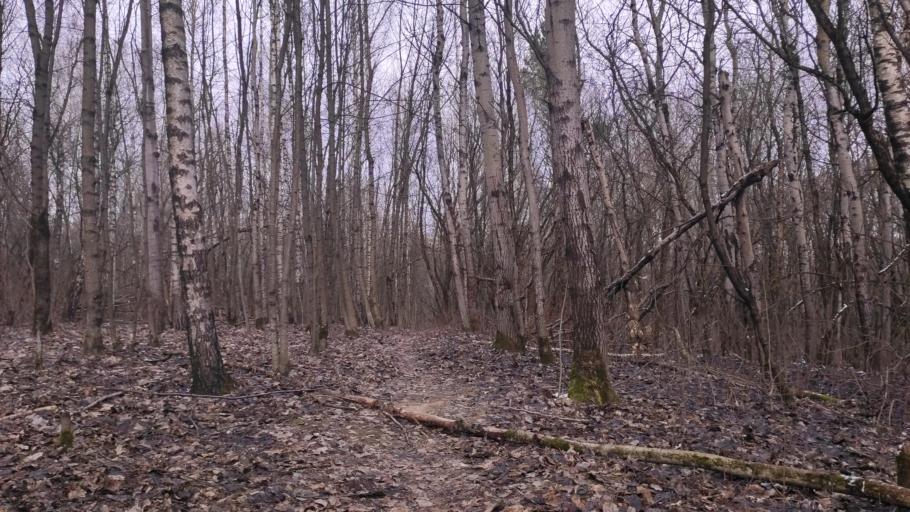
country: BY
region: Minsk
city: Novoye Medvezhino
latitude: 53.8891
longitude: 27.4717
